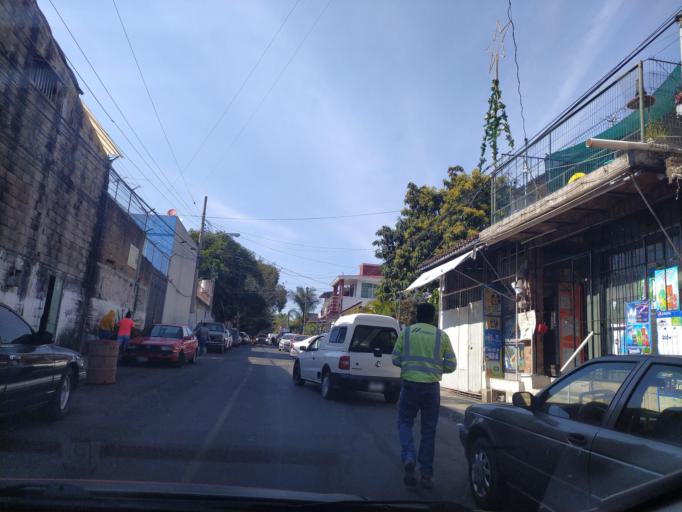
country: MX
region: Jalisco
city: Zapopan2
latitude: 20.6892
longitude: -103.4462
